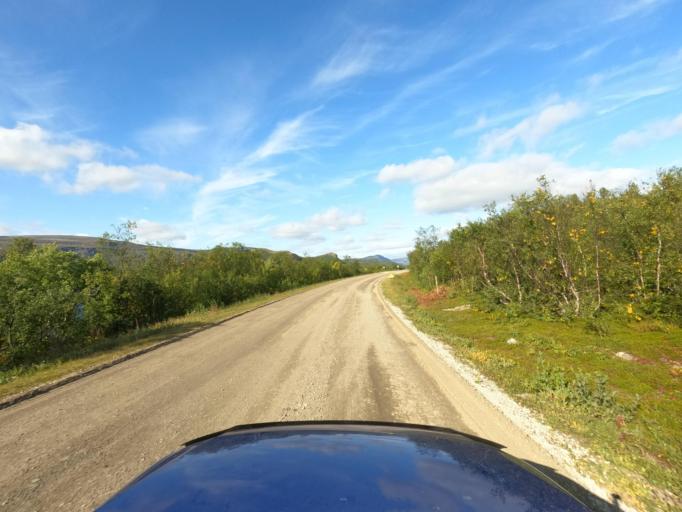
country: NO
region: Finnmark Fylke
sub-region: Porsanger
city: Lakselv
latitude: 69.8936
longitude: 24.9925
